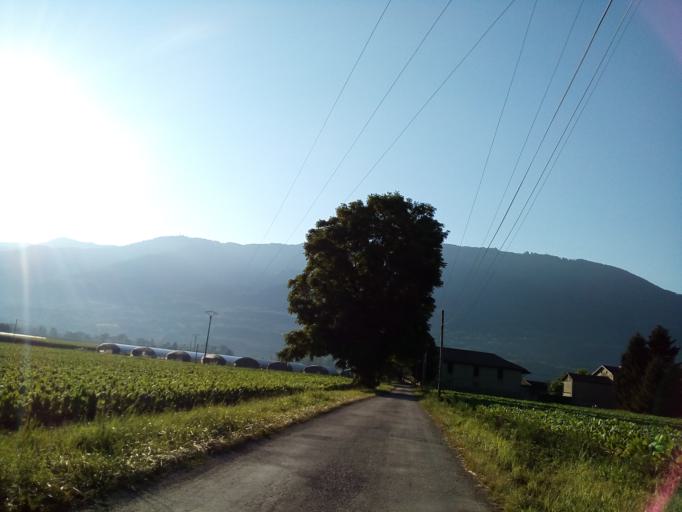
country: FR
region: Rhone-Alpes
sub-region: Departement de l'Isere
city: Barraux
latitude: 45.4079
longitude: 5.9852
